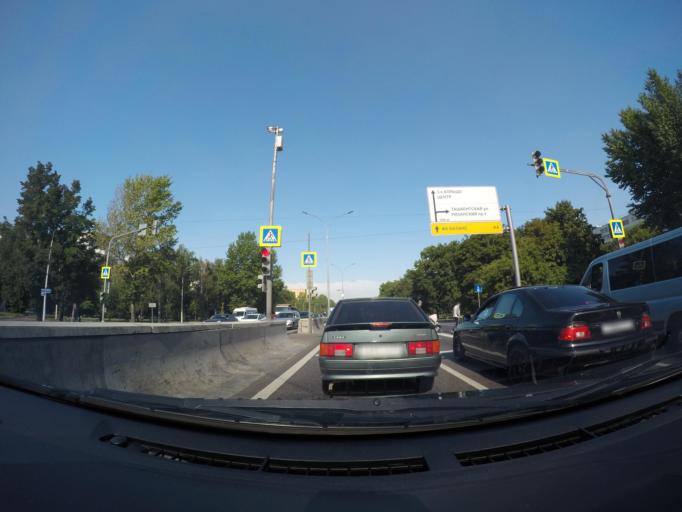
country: RU
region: Moscow
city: Vykhino-Zhulebino
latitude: 55.6957
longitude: 37.8090
